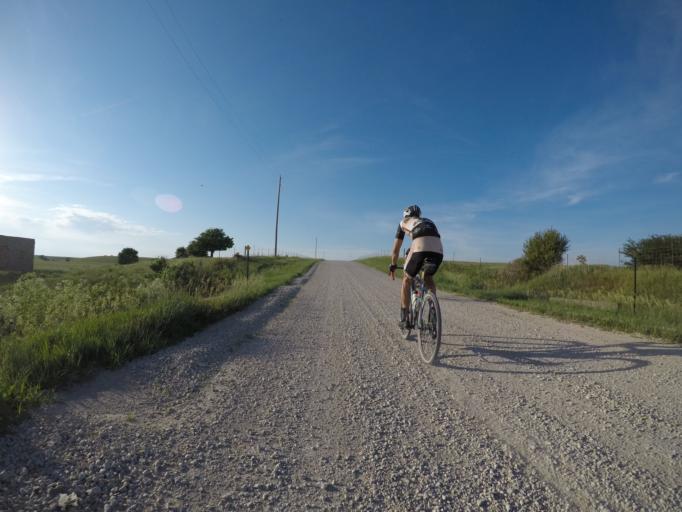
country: US
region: Kansas
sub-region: Riley County
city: Manhattan
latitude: 39.0165
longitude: -96.4918
